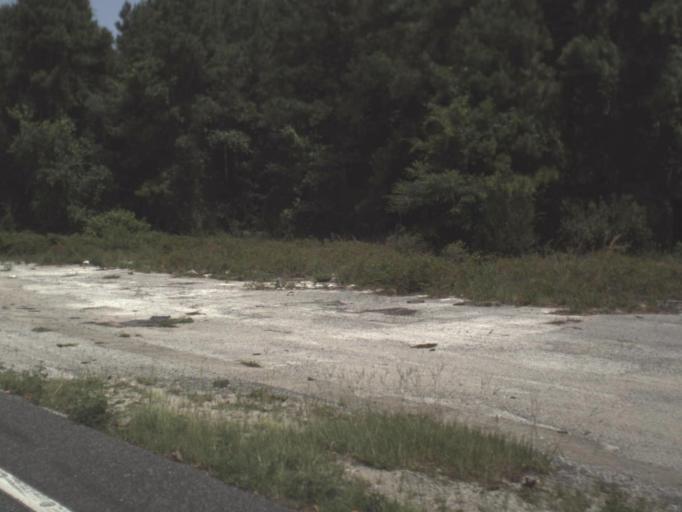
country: US
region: Florida
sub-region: Taylor County
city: Perry
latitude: 30.0158
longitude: -83.5245
